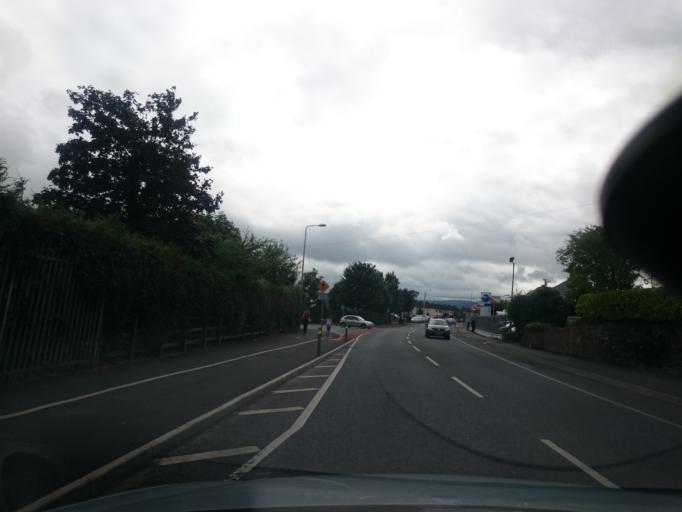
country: IE
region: Leinster
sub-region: County Carlow
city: Carlow
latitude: 52.8381
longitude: -6.9124
